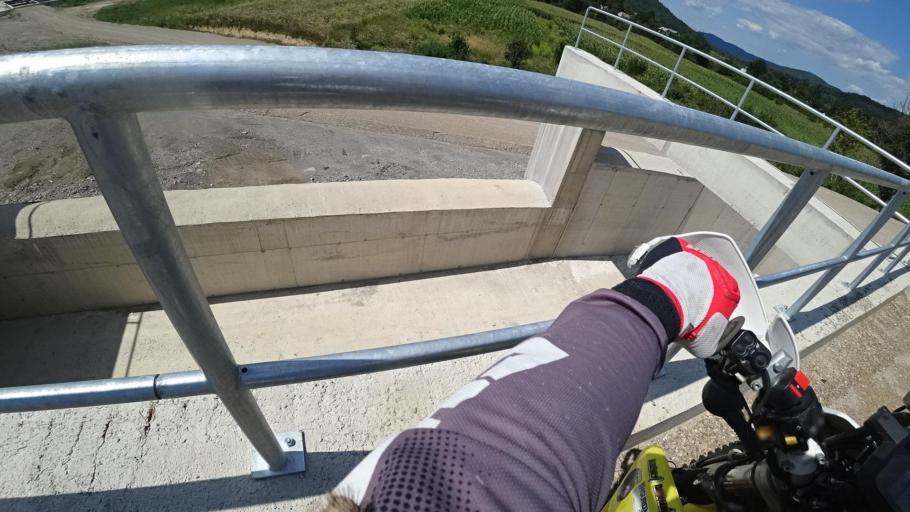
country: HR
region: Karlovacka
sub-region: Grad Ogulin
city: Ogulin
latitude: 45.2798
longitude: 15.1782
